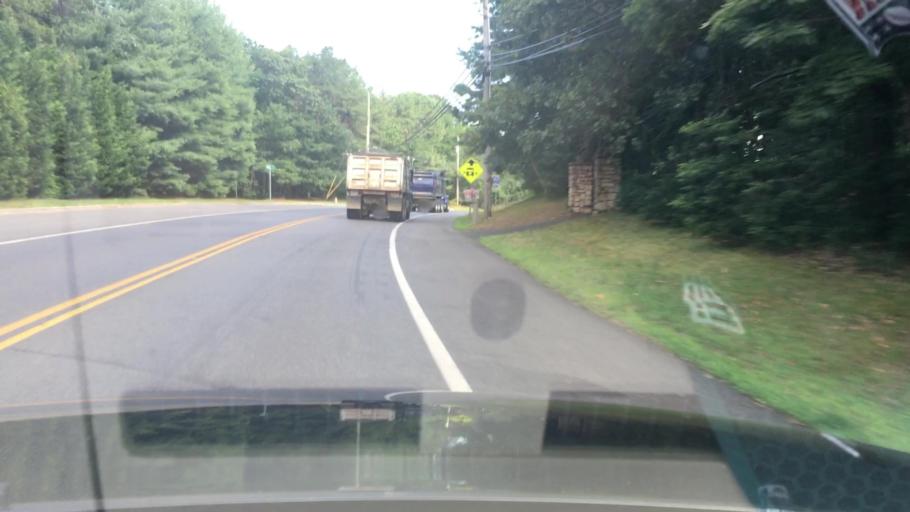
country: US
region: New Jersey
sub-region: Ocean County
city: Vista Center
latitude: 40.1536
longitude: -74.4039
